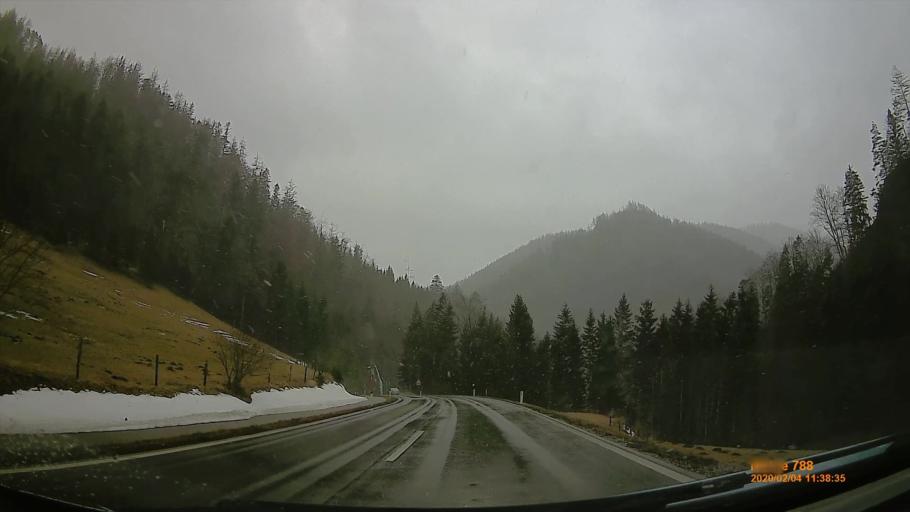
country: AT
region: Styria
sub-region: Politischer Bezirk Bruck-Muerzzuschlag
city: Neuberg an der Muerz
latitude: 47.6638
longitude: 15.5299
